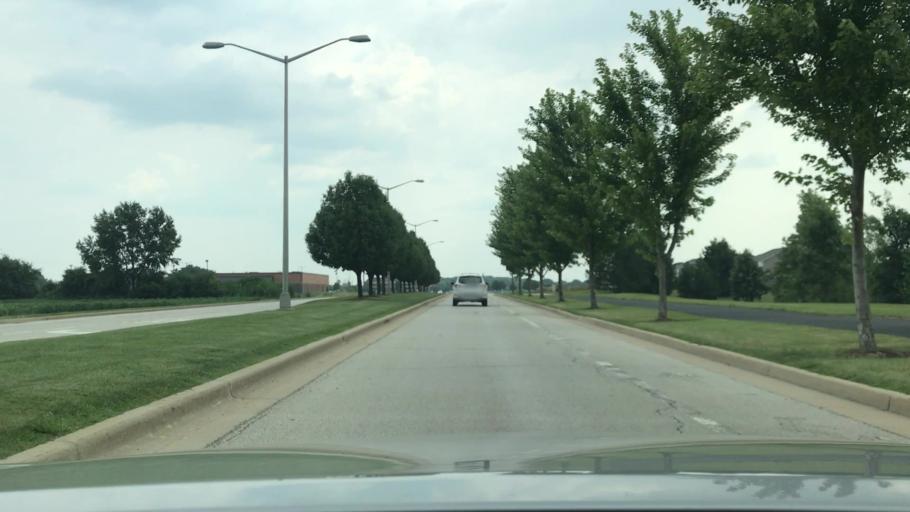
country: US
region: Illinois
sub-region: Will County
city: Plainfield
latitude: 41.6137
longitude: -88.2159
